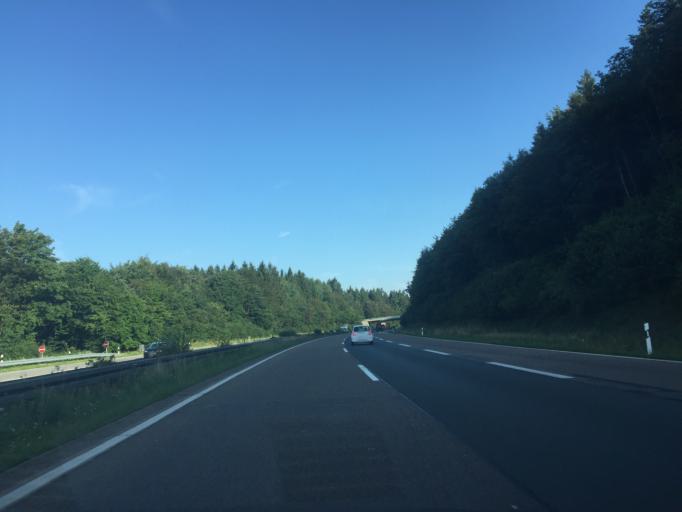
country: DE
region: North Rhine-Westphalia
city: Meinerzhagen
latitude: 51.1541
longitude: 7.6652
